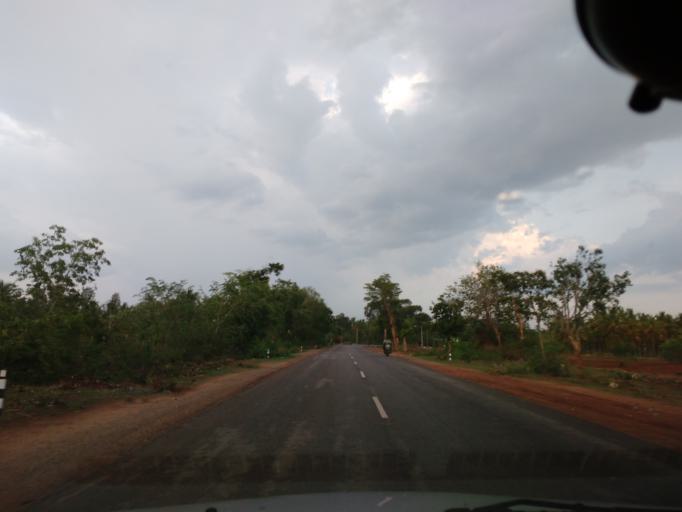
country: IN
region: Karnataka
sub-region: Tumkur
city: Tiptur
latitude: 13.2674
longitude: 76.4380
